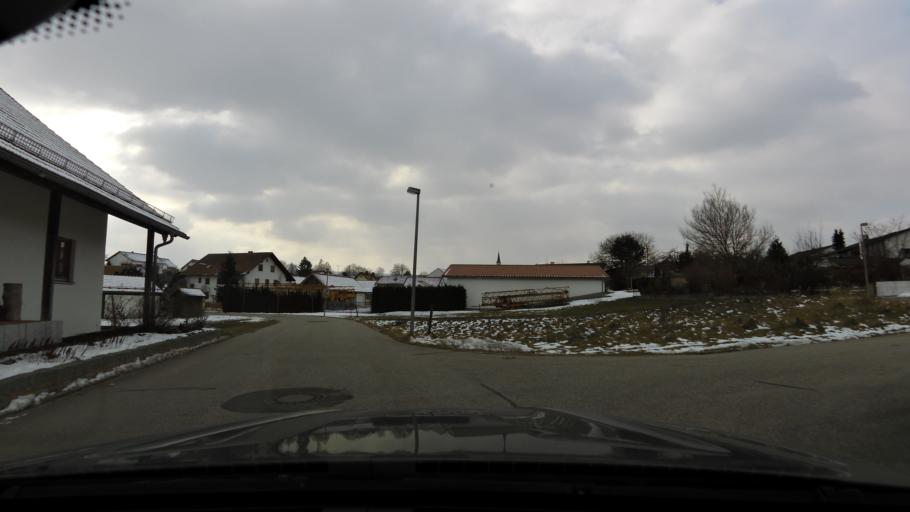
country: DE
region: Bavaria
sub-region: Lower Bavaria
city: Eching
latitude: 48.4740
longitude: 12.0486
